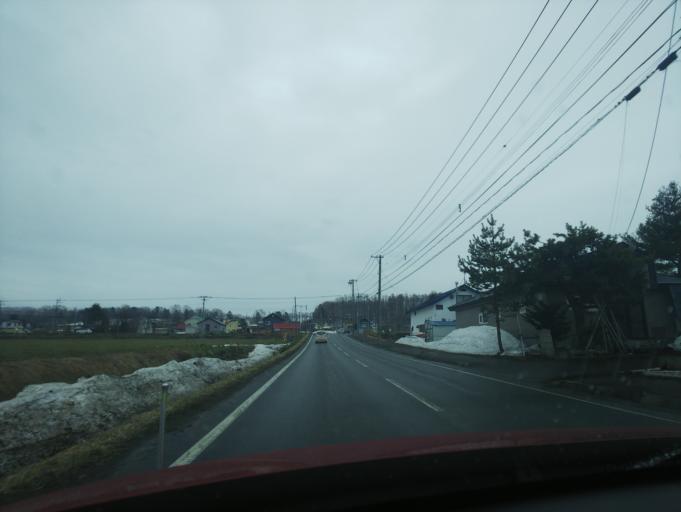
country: JP
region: Hokkaido
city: Nayoro
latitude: 44.3363
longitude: 142.4738
